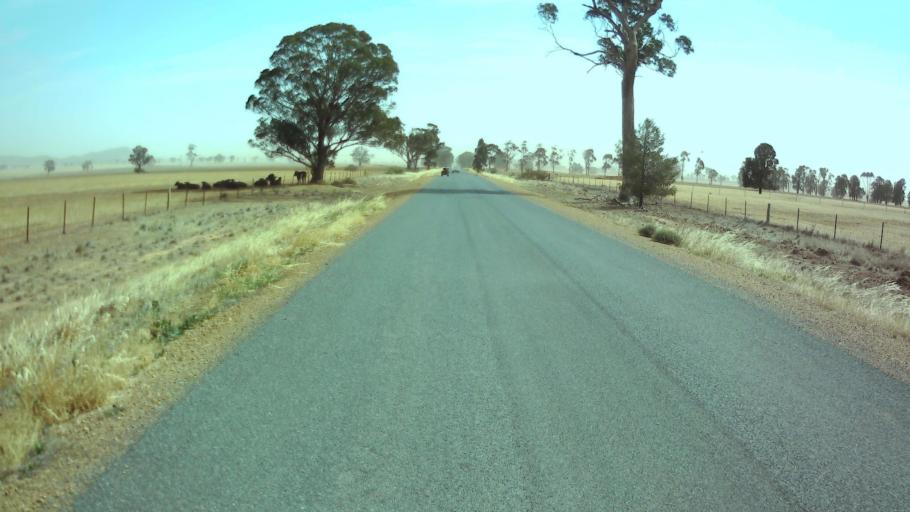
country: AU
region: New South Wales
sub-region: Weddin
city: Grenfell
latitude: -33.7685
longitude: 147.9873
